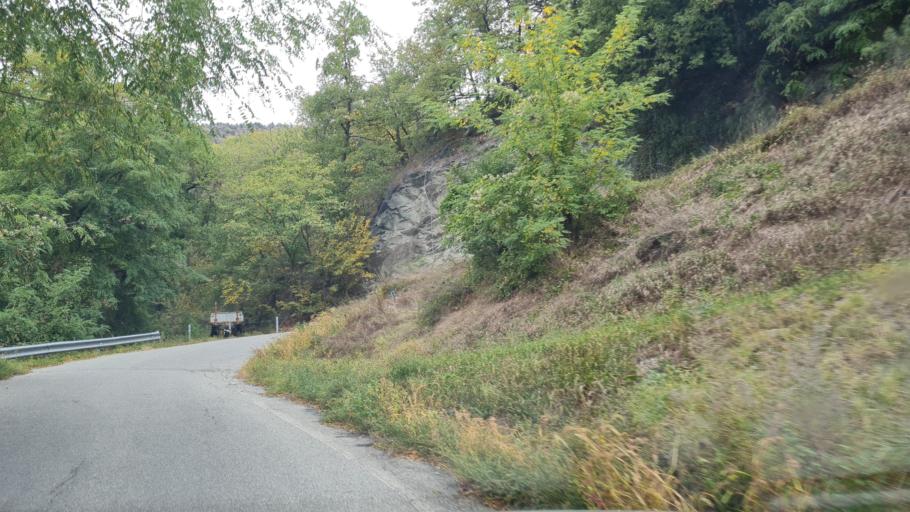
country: IT
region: Aosta Valley
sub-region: Valle d'Aosta
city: Quart
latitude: 45.7452
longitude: 7.4082
